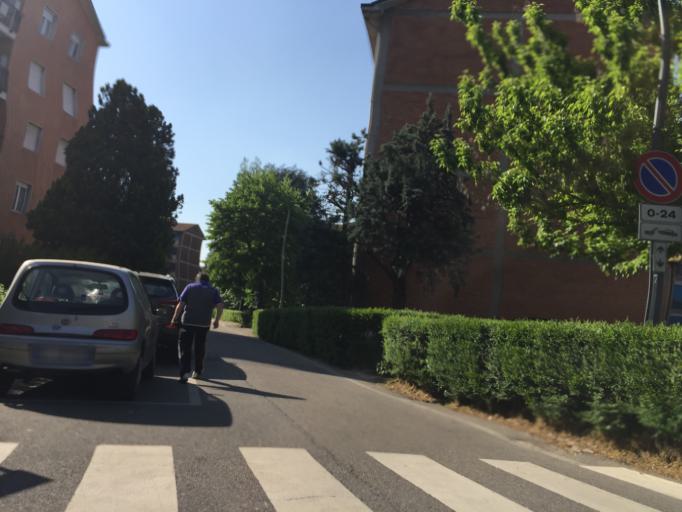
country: IT
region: Lombardy
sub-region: Citta metropolitana di Milano
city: Linate
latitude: 45.4578
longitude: 9.2460
